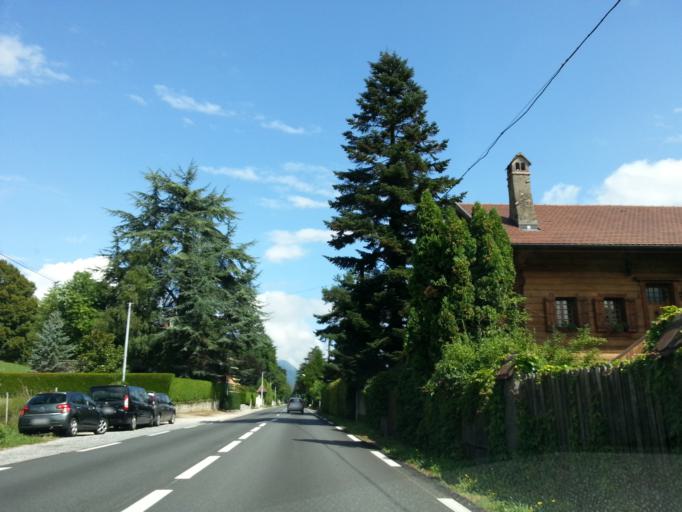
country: FR
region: Rhone-Alpes
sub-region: Departement de la Haute-Savoie
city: Doussard
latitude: 45.7986
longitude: 6.2128
